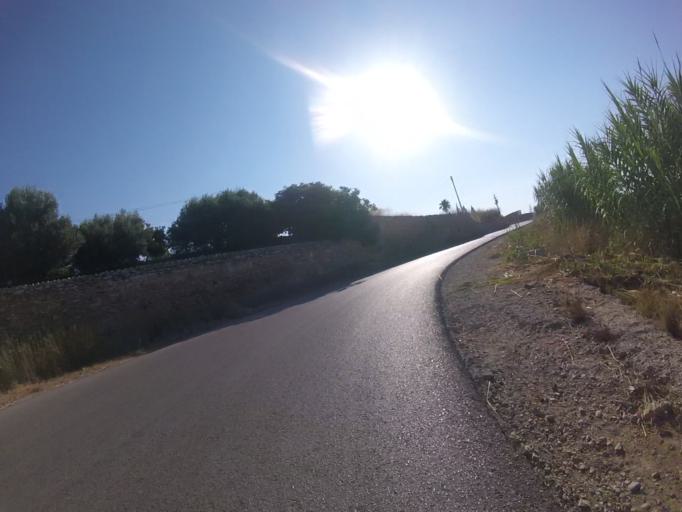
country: ES
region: Valencia
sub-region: Provincia de Castello
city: Benicarlo
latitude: 40.4246
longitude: 0.4316
